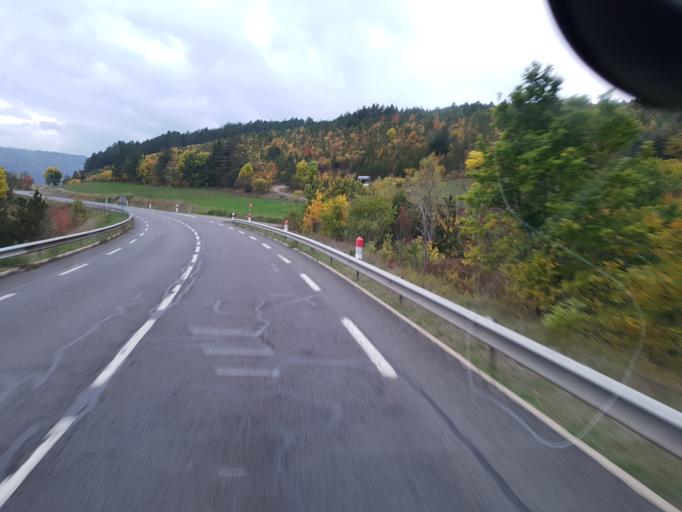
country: FR
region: Languedoc-Roussillon
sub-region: Departement de la Lozere
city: Mende
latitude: 44.5456
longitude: 3.6139
